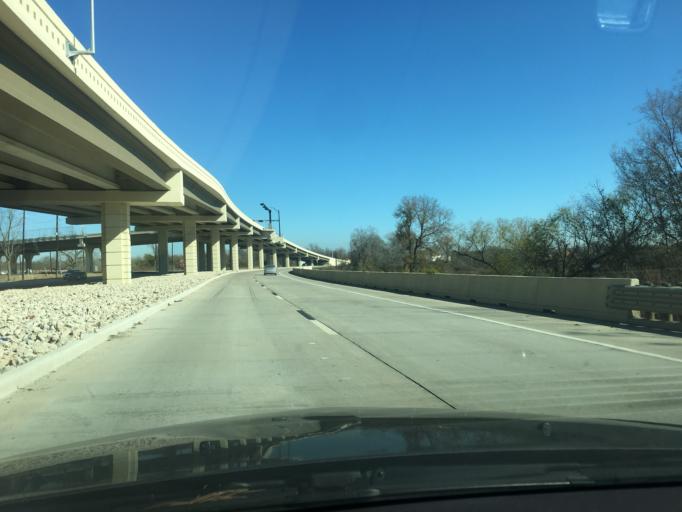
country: US
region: Texas
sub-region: Fort Bend County
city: Richmond
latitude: 29.5931
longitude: -95.7434
